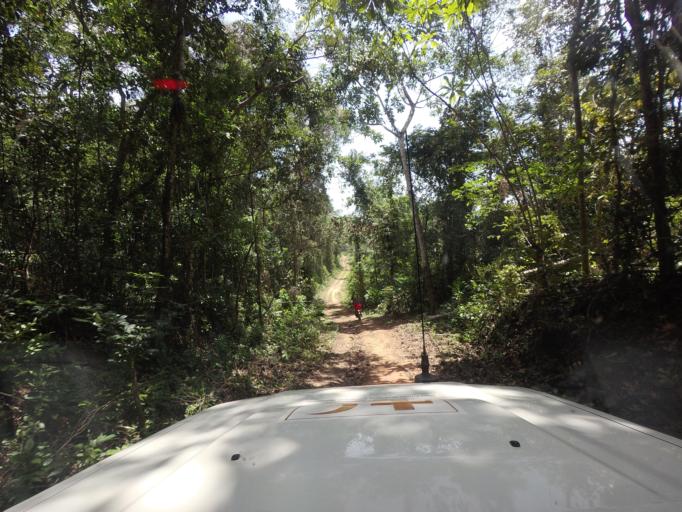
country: GN
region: Nzerekore
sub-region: Yomou
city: Yomou
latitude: 7.3747
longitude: -9.3121
